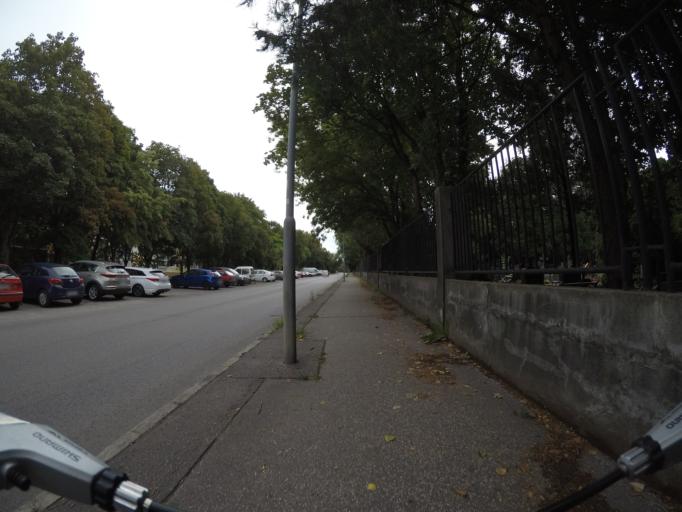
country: SK
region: Bratislavsky
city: Bratislava
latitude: 48.1634
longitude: 17.1623
